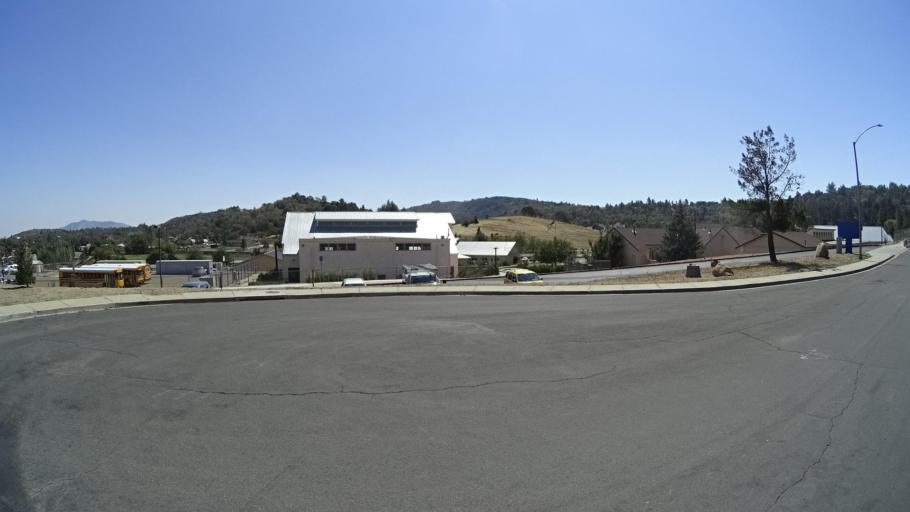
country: US
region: California
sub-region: San Diego County
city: Julian
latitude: 33.0781
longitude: -116.5958
